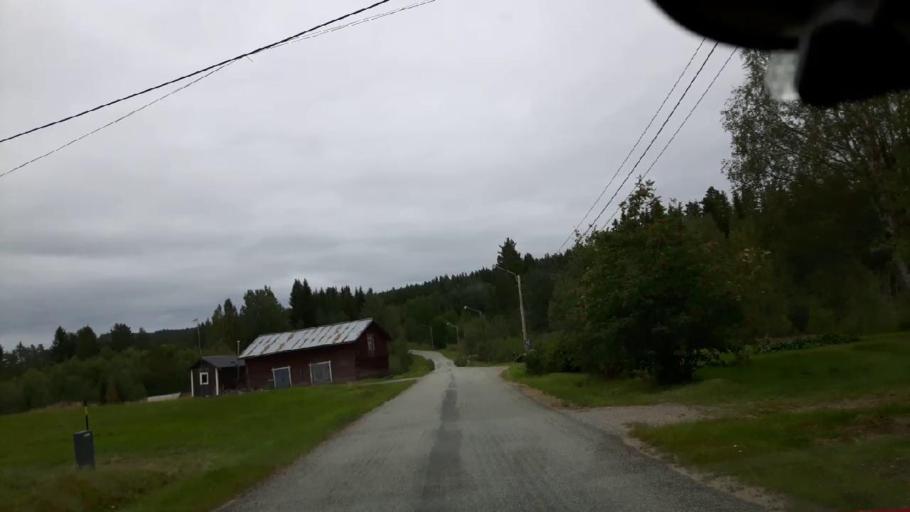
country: SE
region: Vaesternorrland
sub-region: Ange Kommun
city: Fransta
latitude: 62.7746
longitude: 15.9891
